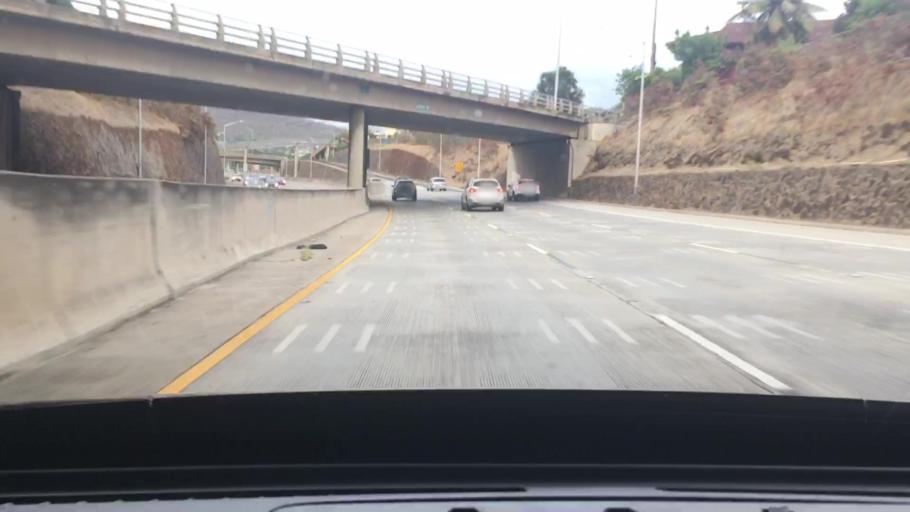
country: US
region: Hawaii
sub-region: Honolulu County
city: Honolulu
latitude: 21.2785
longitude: -157.7951
